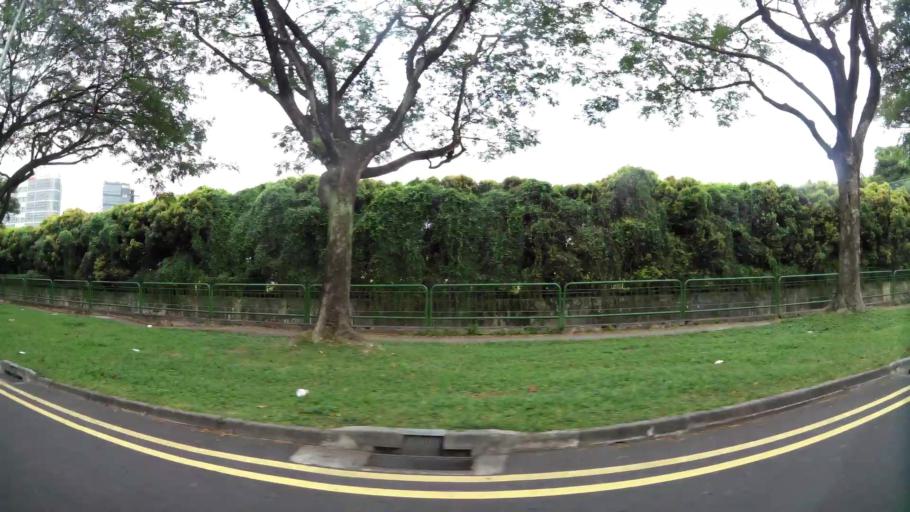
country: SG
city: Singapore
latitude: 1.3467
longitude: 103.8394
